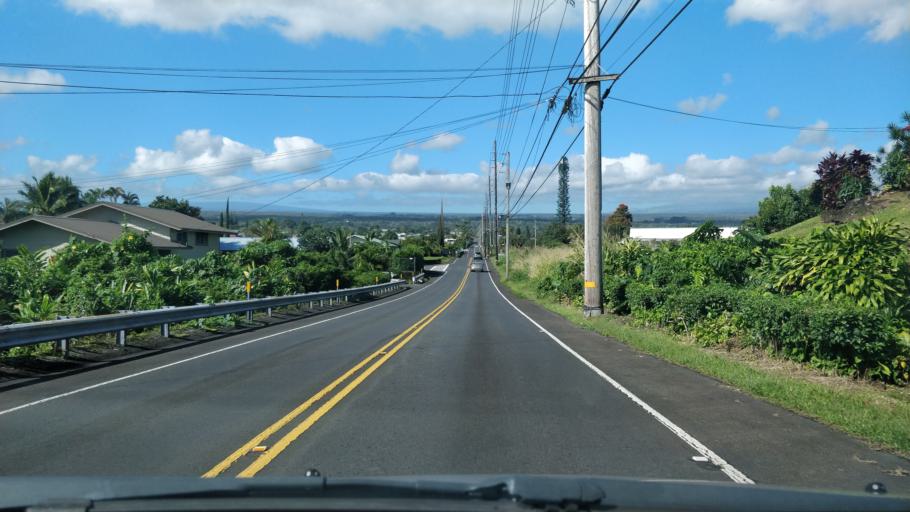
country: US
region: Hawaii
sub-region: Hawaii County
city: Hilo
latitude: 19.6829
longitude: -155.0927
